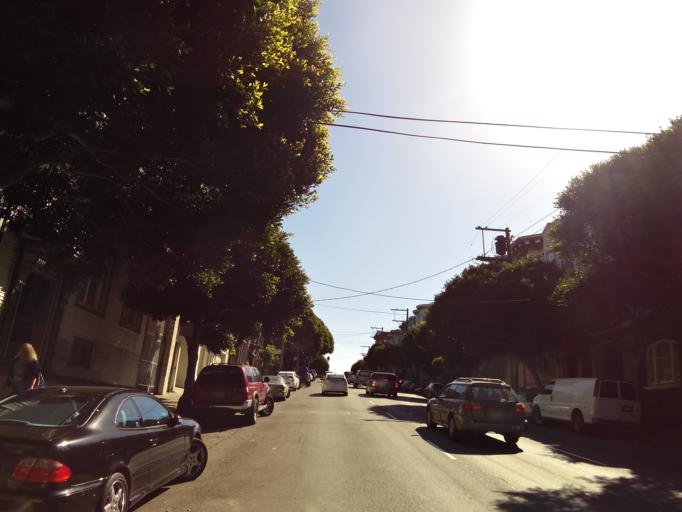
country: US
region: California
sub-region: San Francisco County
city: San Francisco
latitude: 37.7737
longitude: -122.4339
